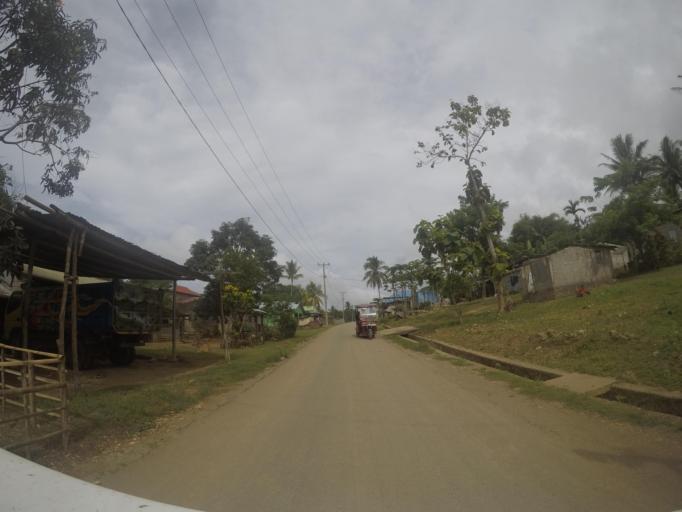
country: TL
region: Lautem
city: Lospalos
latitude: -8.5064
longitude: 126.9738
